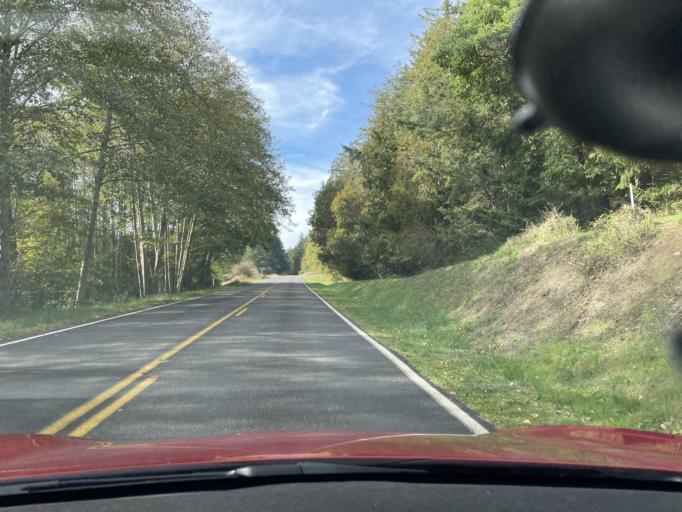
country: US
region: Washington
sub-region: San Juan County
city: Friday Harbor
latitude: 48.5290
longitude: -122.9831
